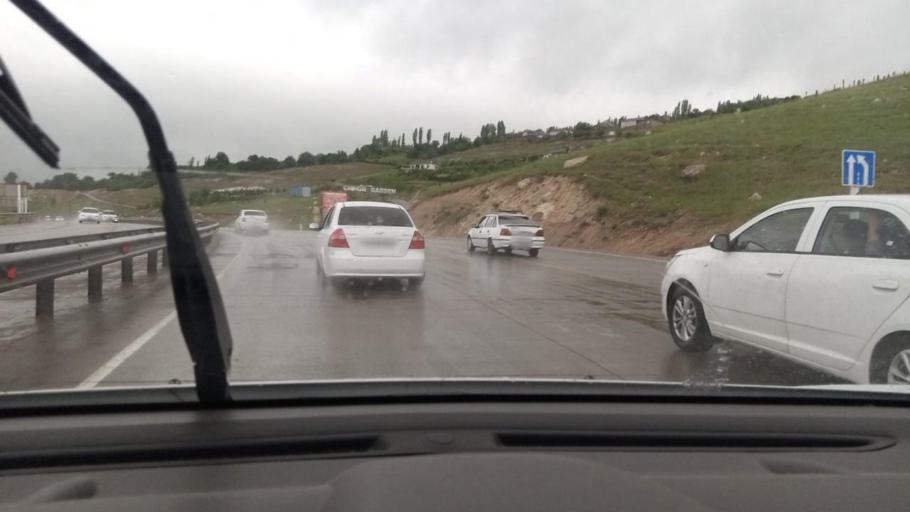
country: UZ
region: Toshkent
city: Angren
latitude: 41.0739
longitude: 70.2678
